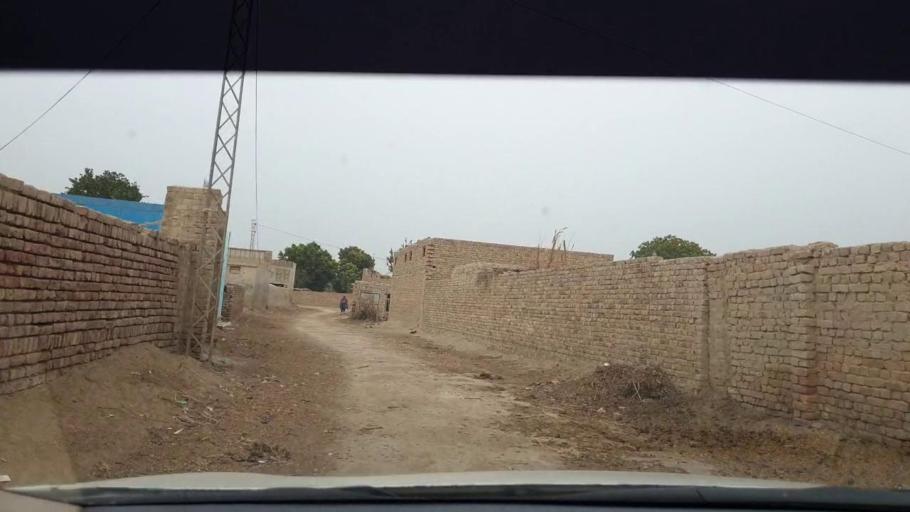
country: PK
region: Sindh
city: Berani
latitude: 25.8859
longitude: 68.8073
